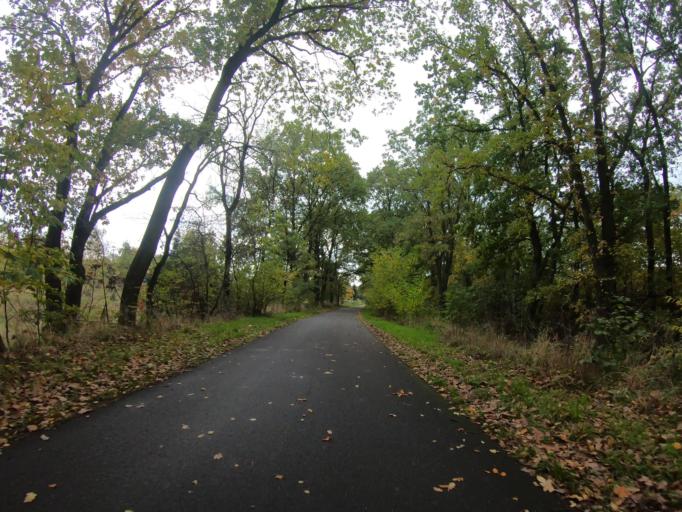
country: DE
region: Lower Saxony
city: Isenbuttel
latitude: 52.4456
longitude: 10.5731
